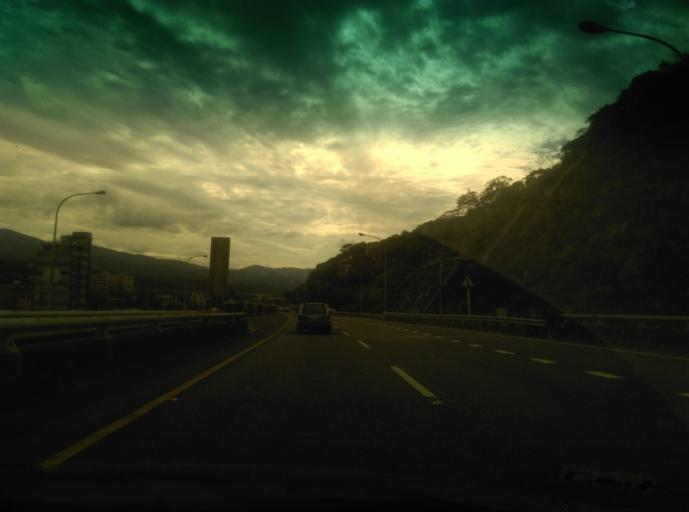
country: TW
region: Taiwan
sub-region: Keelung
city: Keelung
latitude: 25.1149
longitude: 121.7282
